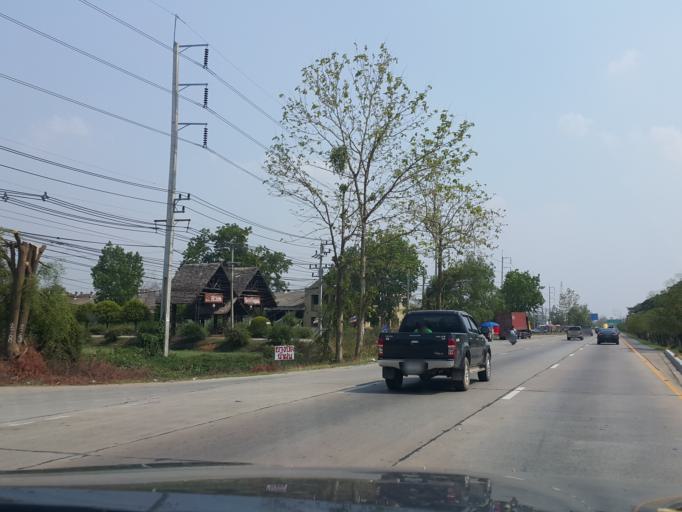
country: TH
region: Lamphun
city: Lamphun
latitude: 18.6228
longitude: 99.0477
